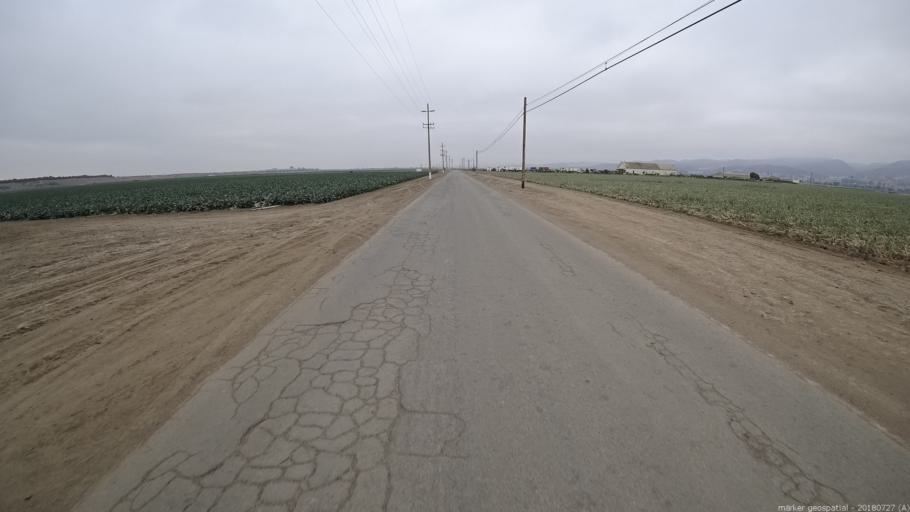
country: US
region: California
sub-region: Monterey County
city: King City
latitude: 36.2493
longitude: -121.1489
